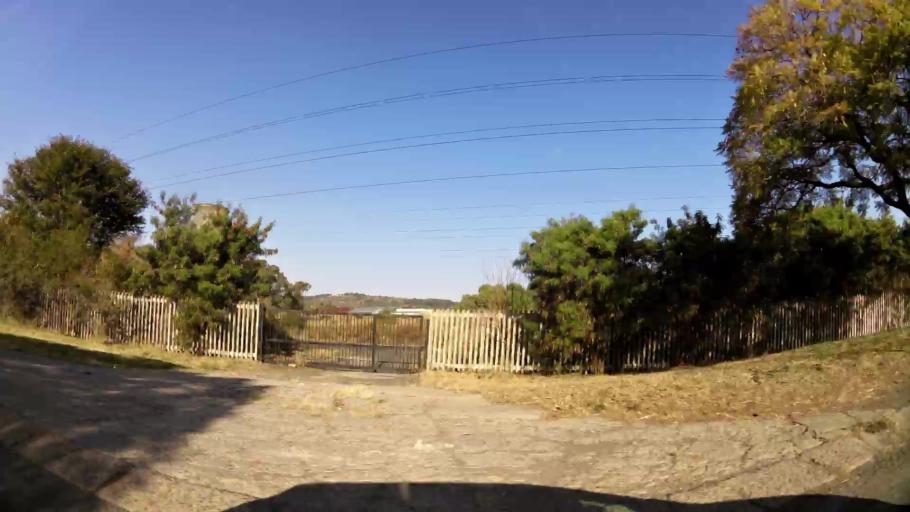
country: ZA
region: Gauteng
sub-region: City of Tshwane Metropolitan Municipality
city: Pretoria
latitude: -25.7584
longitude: 28.1415
